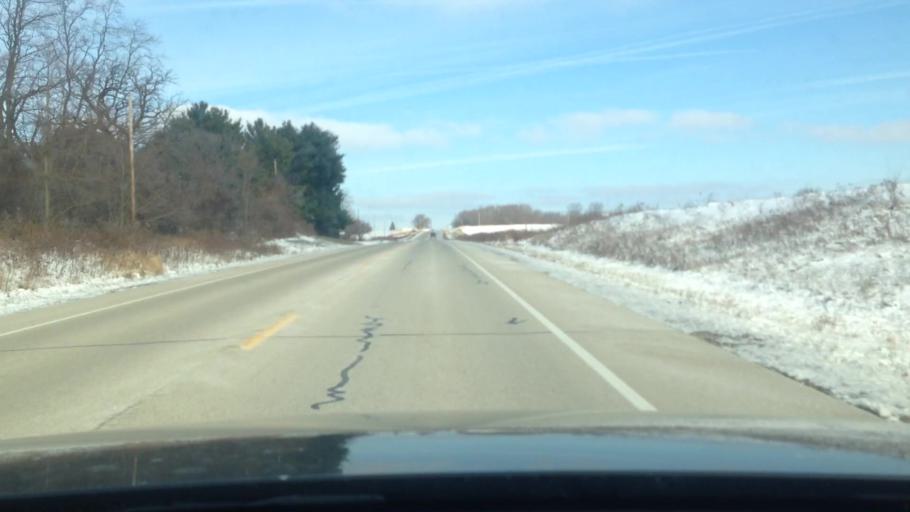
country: US
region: Wisconsin
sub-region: Walworth County
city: East Troy
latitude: 42.7392
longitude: -88.4060
